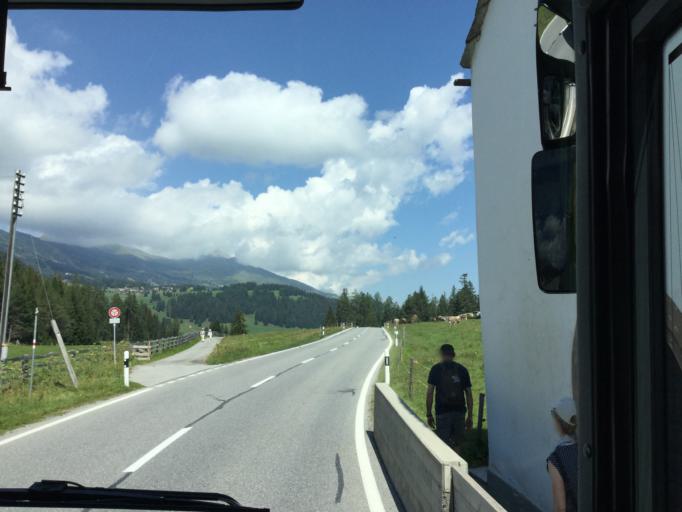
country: CH
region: Grisons
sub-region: Albula District
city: Tiefencastel
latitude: 46.6956
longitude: 9.5589
